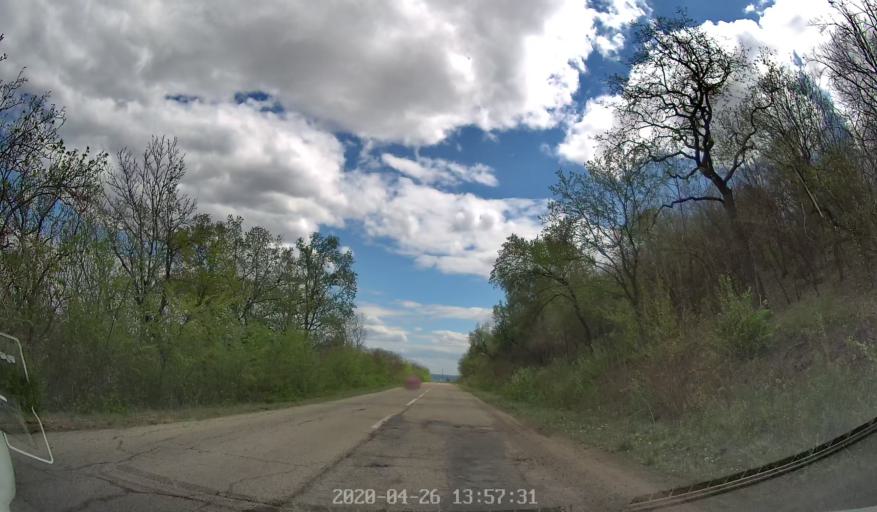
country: MD
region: Telenesti
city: Cocieri
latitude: 47.2738
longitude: 29.1165
